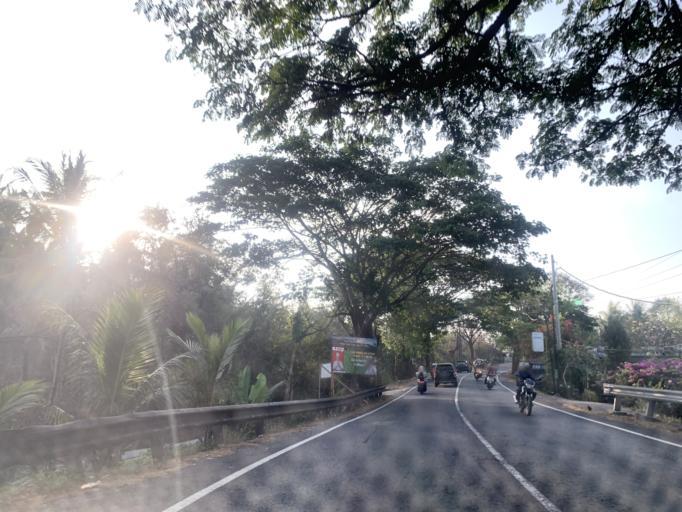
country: ID
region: Bali
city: Banjar Delodrurung
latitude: -8.5019
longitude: 115.0224
